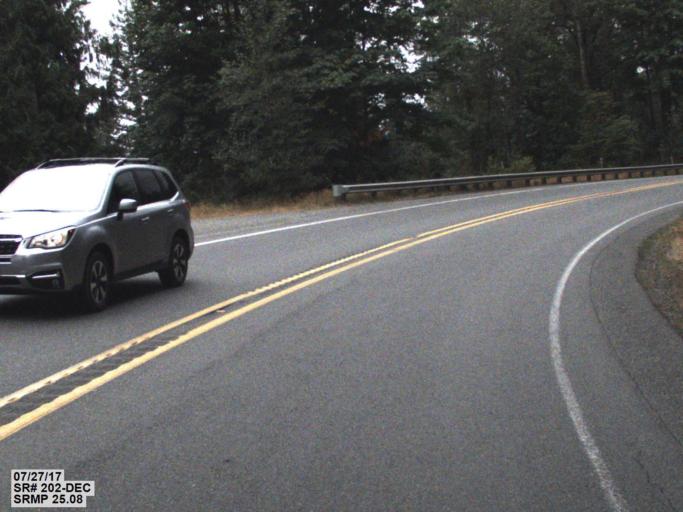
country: US
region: Washington
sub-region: King County
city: Snoqualmie
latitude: 47.5505
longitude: -121.8401
